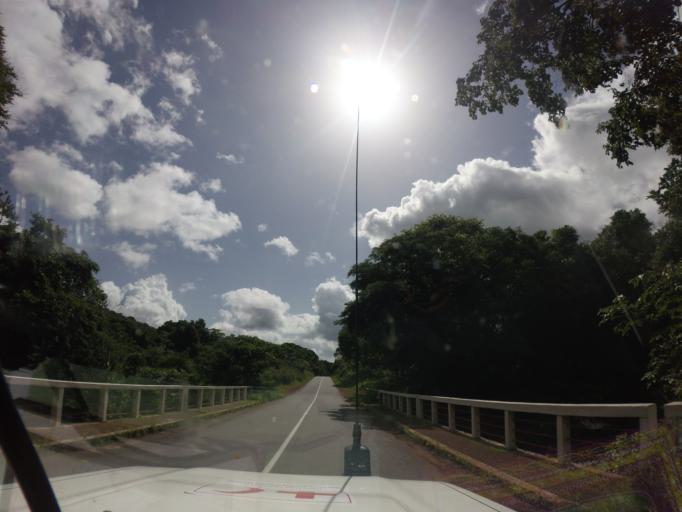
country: GN
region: Mamou
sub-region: Mamou Prefecture
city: Mamou
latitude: 10.3341
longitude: -12.0288
